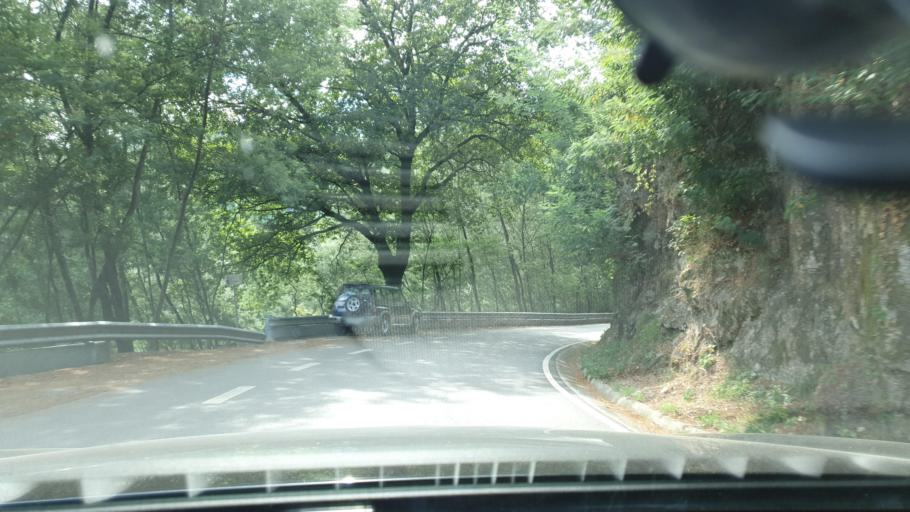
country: PT
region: Braga
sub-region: Vieira do Minho
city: Vieira do Minho
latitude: 41.6876
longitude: -8.0936
